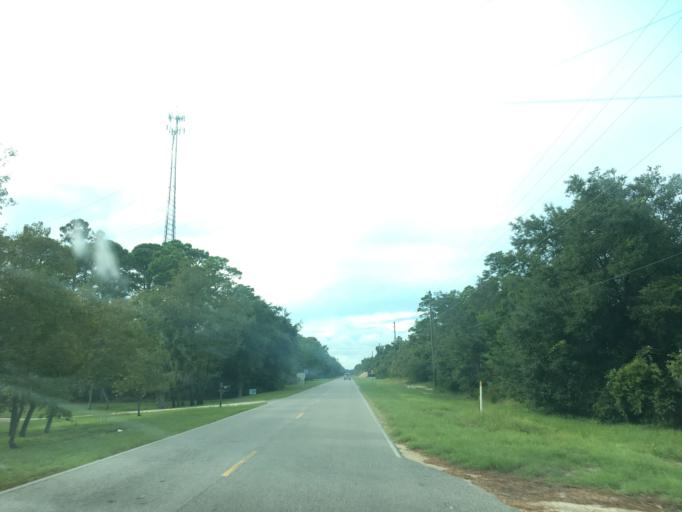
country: US
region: Florida
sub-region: Wakulla County
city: Crawfordville
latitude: 29.9151
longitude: -84.3679
